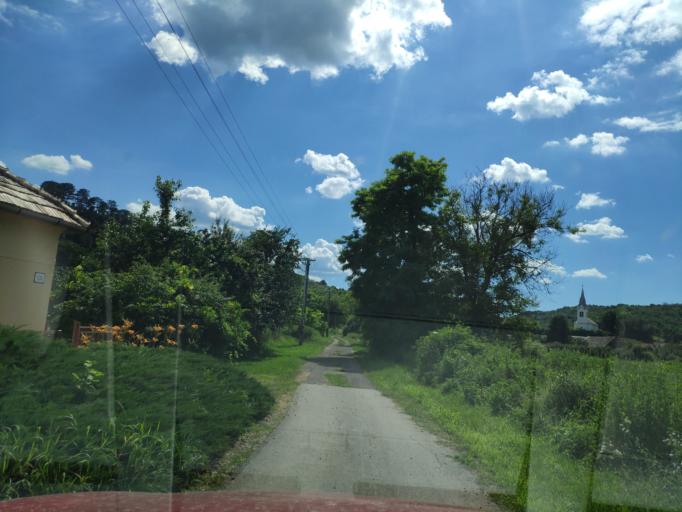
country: HU
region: Borsod-Abauj-Zemplen
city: Arlo
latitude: 48.2787
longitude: 20.1897
